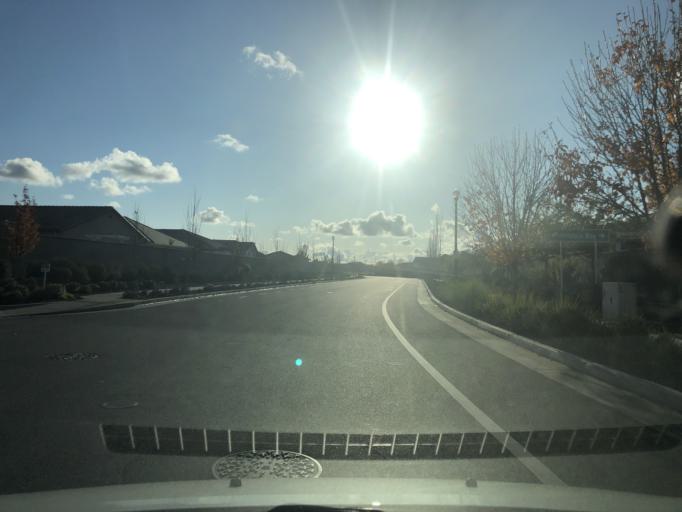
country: US
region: California
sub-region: Sacramento County
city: Antelope
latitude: 38.7740
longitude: -121.3797
